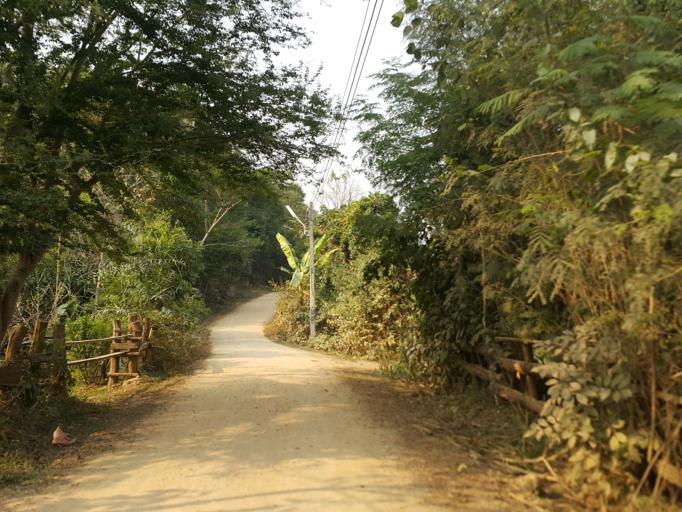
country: TH
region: Lamphun
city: Li
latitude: 17.6058
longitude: 98.9641
